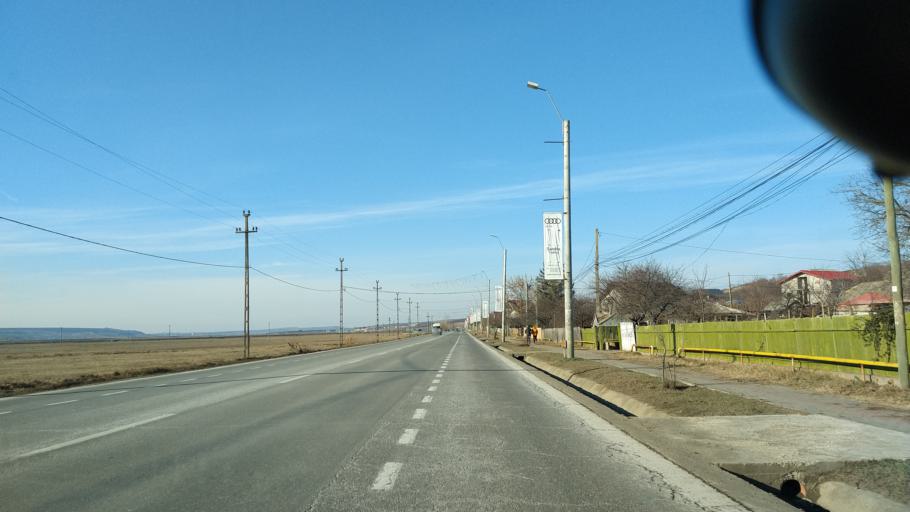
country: RO
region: Iasi
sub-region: Comuna Letcani
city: Letcani
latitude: 47.1991
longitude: 27.3912
